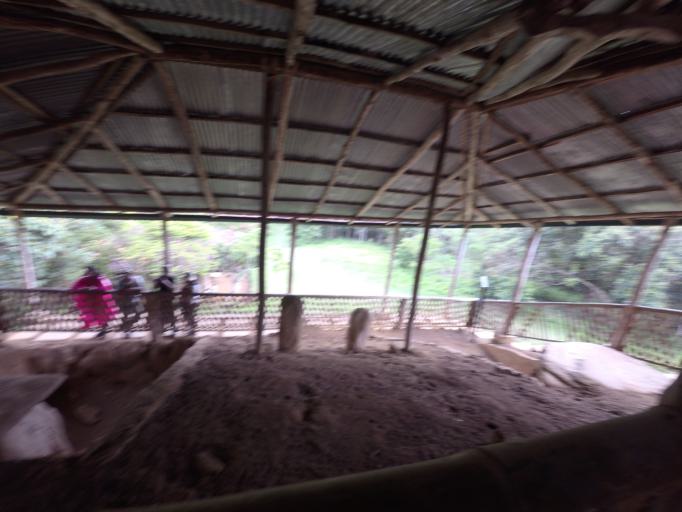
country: CO
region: Huila
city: San Agustin
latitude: 1.9131
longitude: -76.2949
